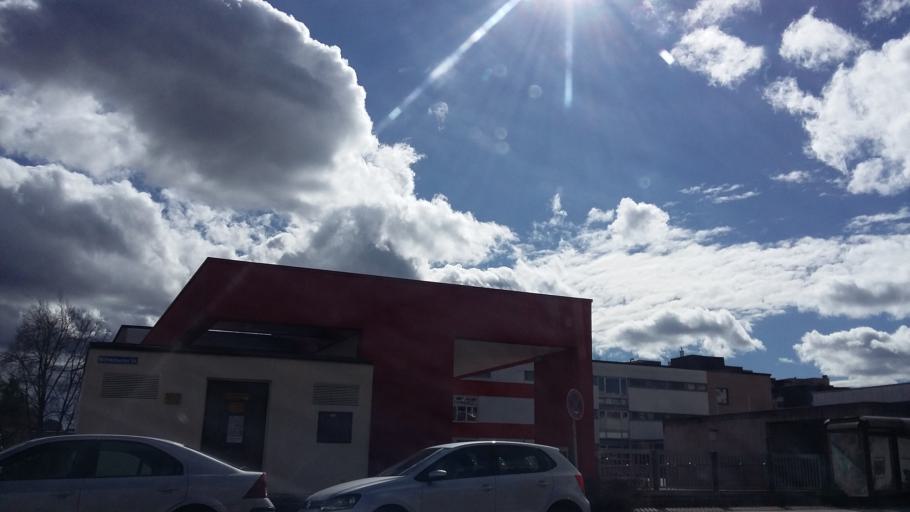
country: DE
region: Bavaria
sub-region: Upper Bavaria
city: Germering
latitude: 48.1360
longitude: 11.3782
